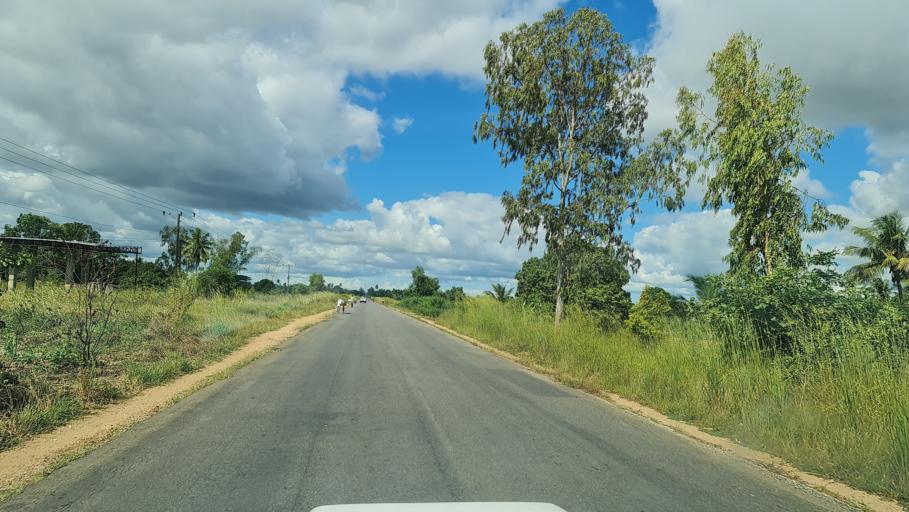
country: MZ
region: Zambezia
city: Quelimane
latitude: -17.5927
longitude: 36.7724
